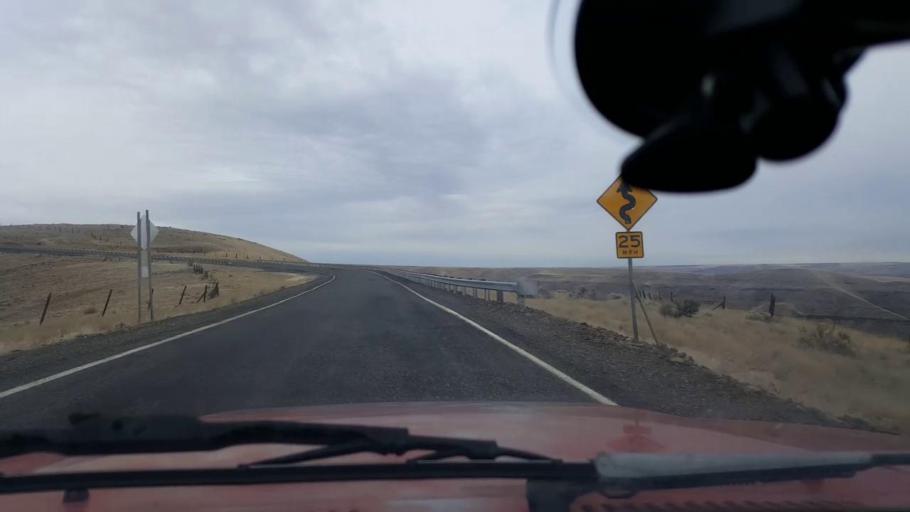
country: US
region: Washington
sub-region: Asotin County
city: Clarkston Heights-Vineland
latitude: 46.3339
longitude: -117.2984
